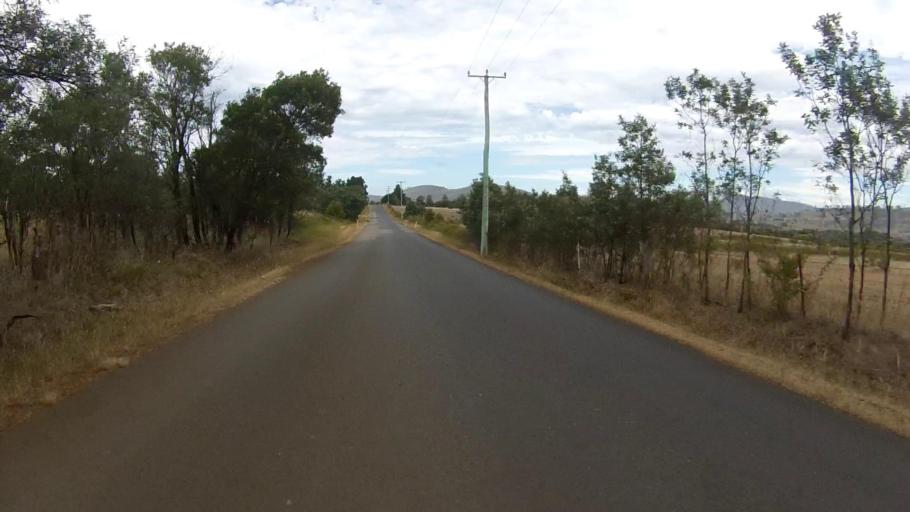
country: AU
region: Tasmania
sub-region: Clarence
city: Cambridge
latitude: -42.7151
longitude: 147.4526
